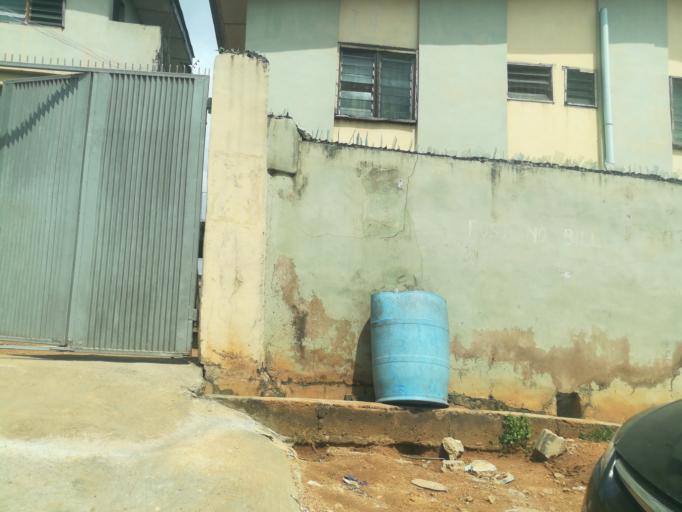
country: NG
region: Oyo
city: Ibadan
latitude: 7.3570
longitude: 3.8798
